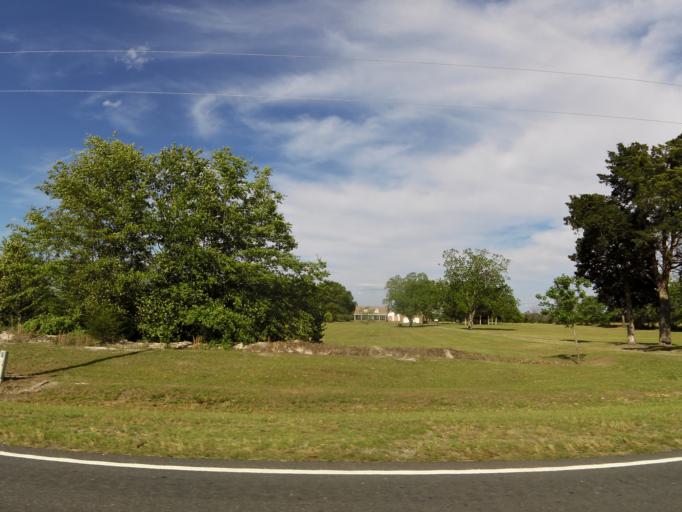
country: US
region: South Carolina
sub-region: Allendale County
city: Fairfax
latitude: 33.0203
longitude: -81.2176
